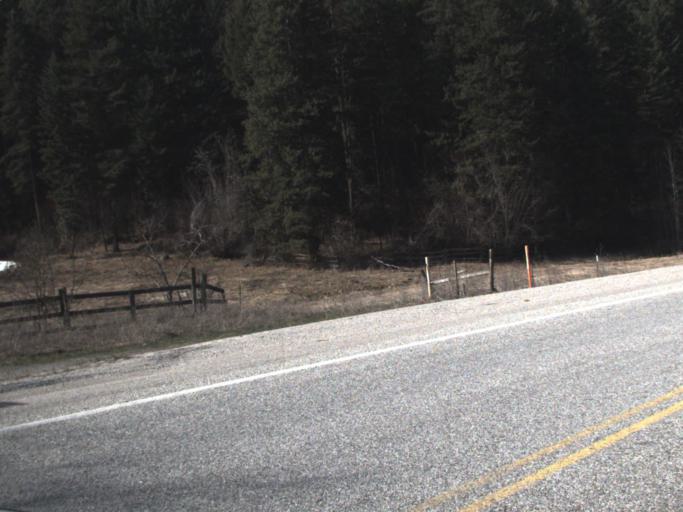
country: US
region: Washington
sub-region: Stevens County
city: Colville
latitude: 48.5127
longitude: -117.7747
